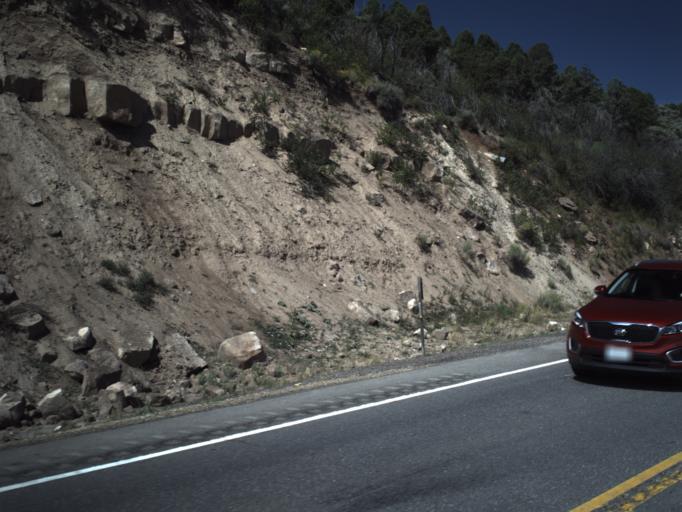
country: US
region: Utah
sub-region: Carbon County
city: Helper
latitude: 39.8174
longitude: -110.9402
